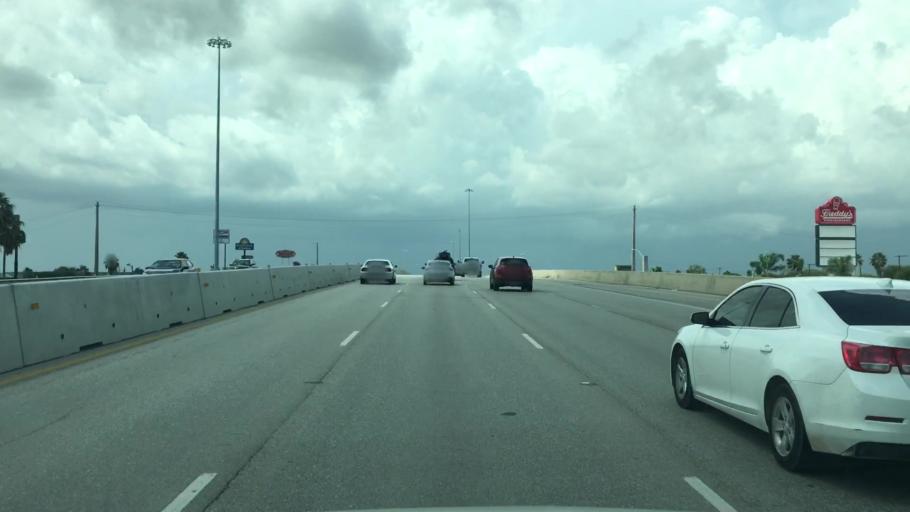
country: US
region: Texas
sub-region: Nueces County
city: Corpus Christi
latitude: 27.7209
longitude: -97.3969
